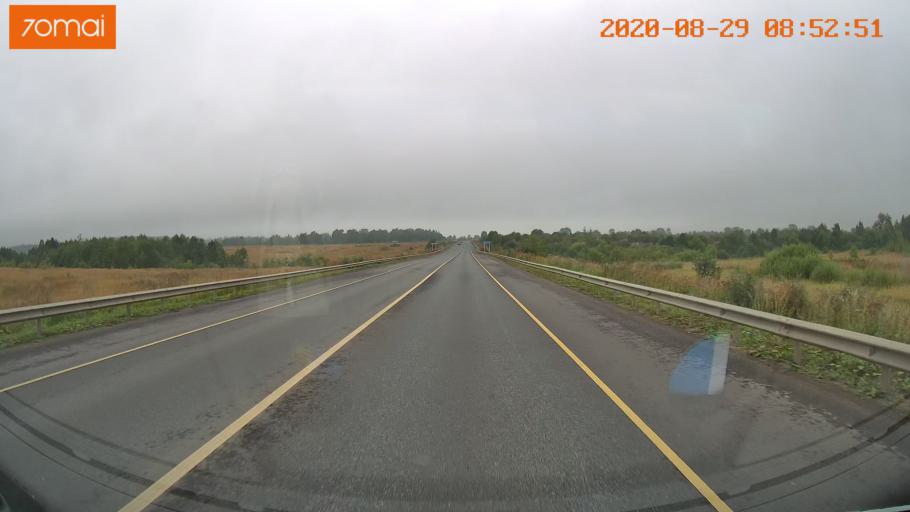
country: RU
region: Ivanovo
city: Staraya Vichuga
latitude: 57.2149
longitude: 41.8643
